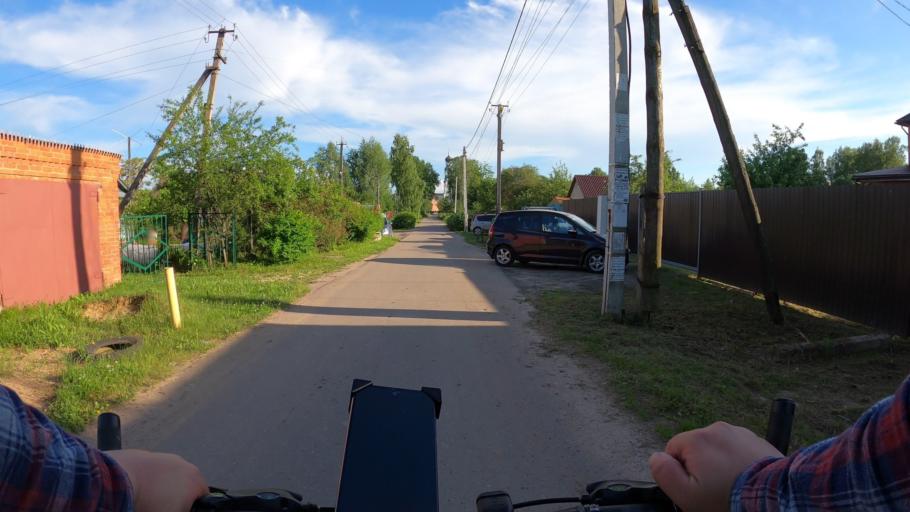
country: RU
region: Moskovskaya
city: Ashitkovo
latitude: 55.4419
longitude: 38.6055
